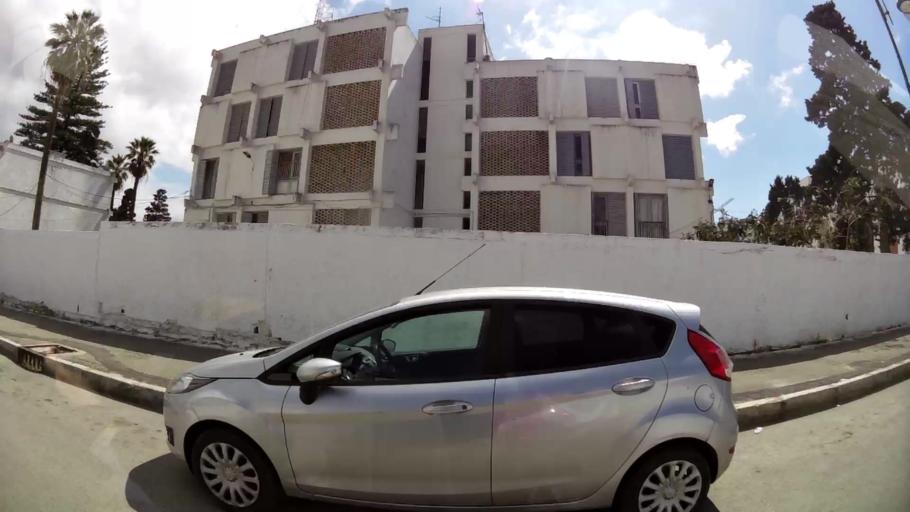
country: MA
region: Tanger-Tetouan
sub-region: Tanger-Assilah
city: Tangier
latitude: 35.7675
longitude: -5.8114
